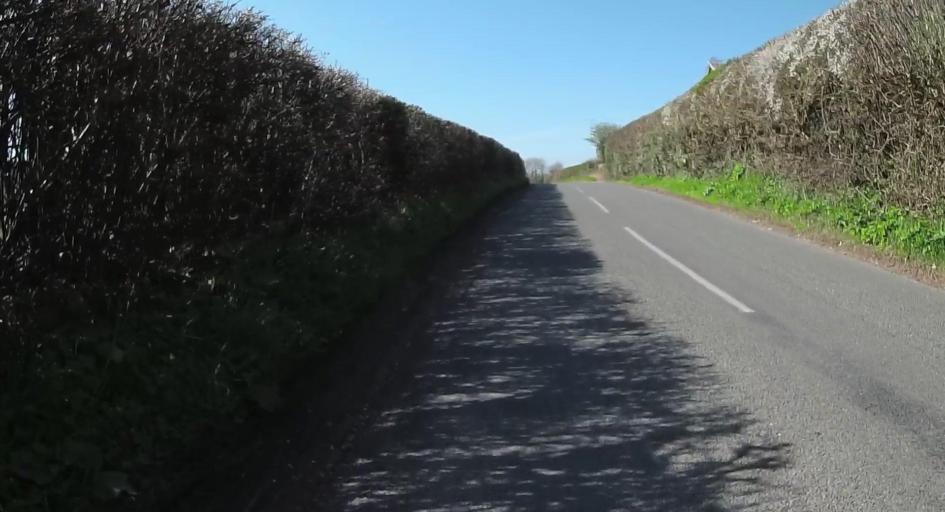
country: GB
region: England
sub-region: Hampshire
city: Andover
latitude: 51.2703
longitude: -1.4371
